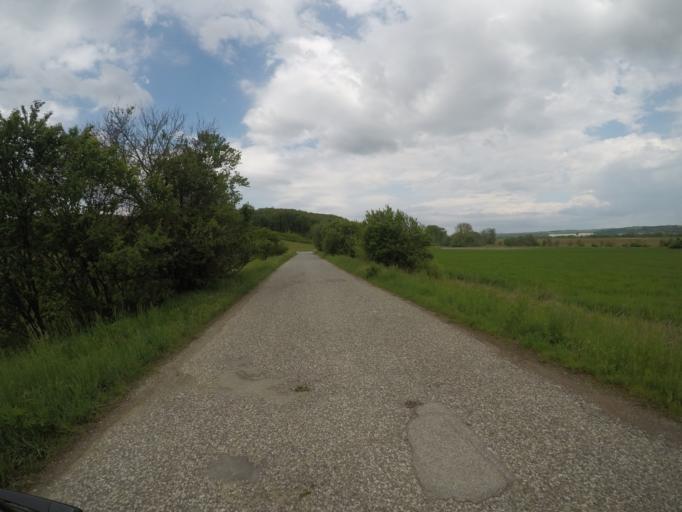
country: SK
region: Nitriansky
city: Sahy
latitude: 48.0878
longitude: 18.8681
